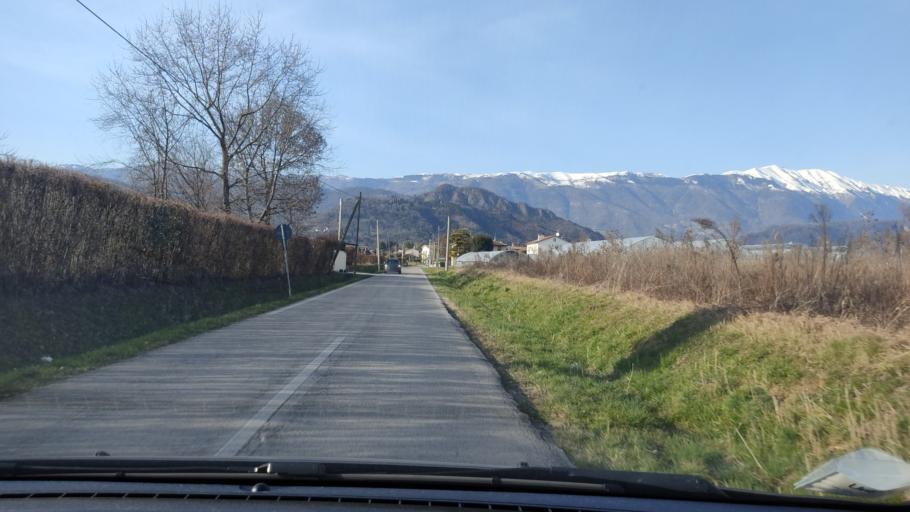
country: IT
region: Veneto
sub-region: Provincia di Treviso
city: Vittorio Veneto
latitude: 45.9653
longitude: 12.3045
